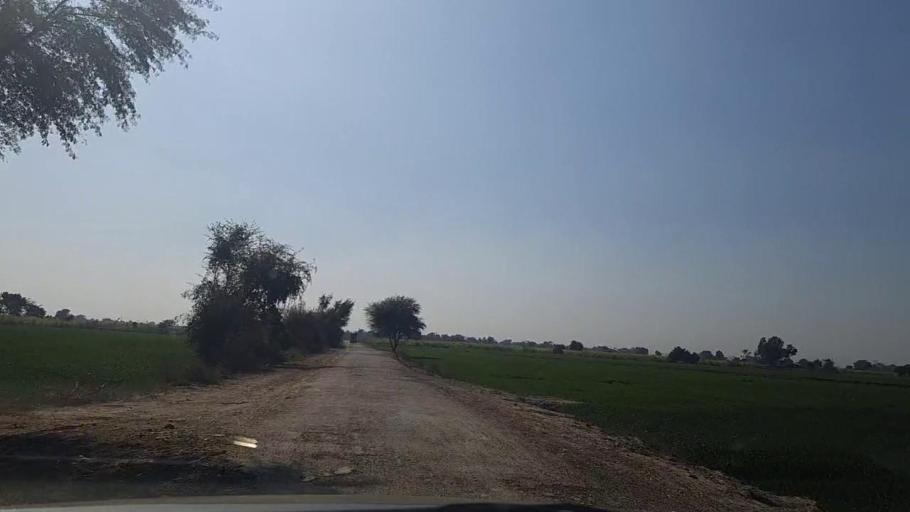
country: PK
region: Sindh
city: Daulatpur
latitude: 26.2831
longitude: 68.0427
